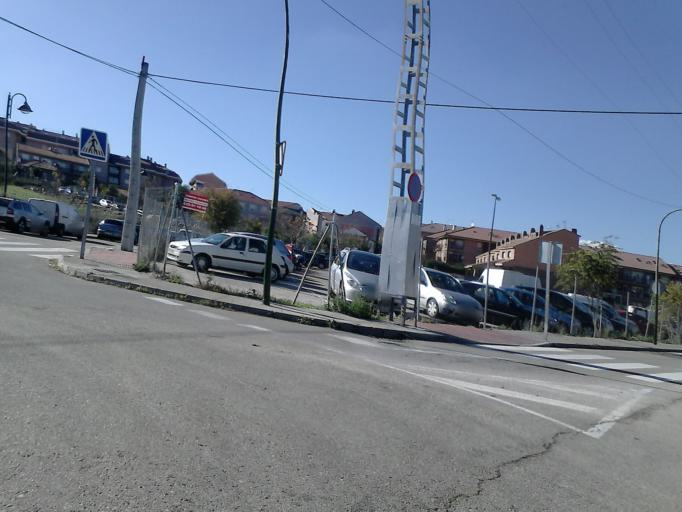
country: ES
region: Madrid
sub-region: Provincia de Madrid
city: Galapagar
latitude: 40.5750
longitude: -3.9991
